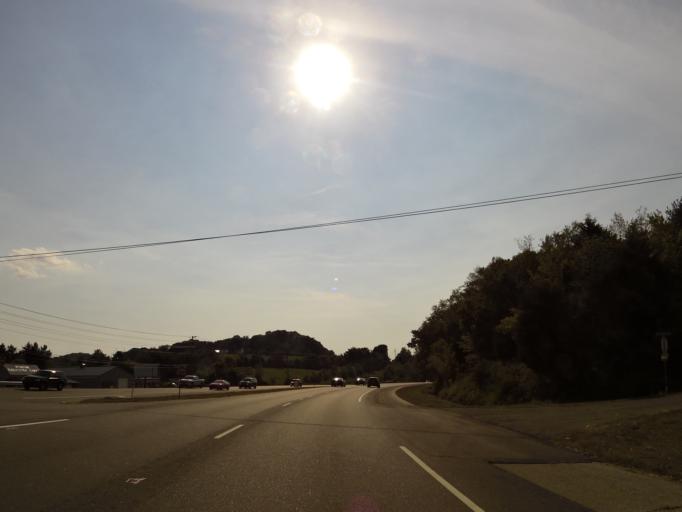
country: US
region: Tennessee
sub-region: Blount County
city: Louisville
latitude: 35.7552
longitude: -84.0772
